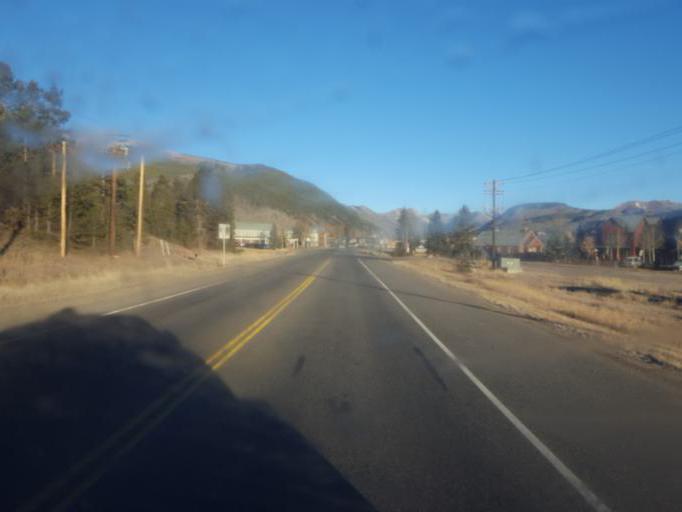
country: US
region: Colorado
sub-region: Gunnison County
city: Crested Butte
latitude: 38.8653
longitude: -106.9784
